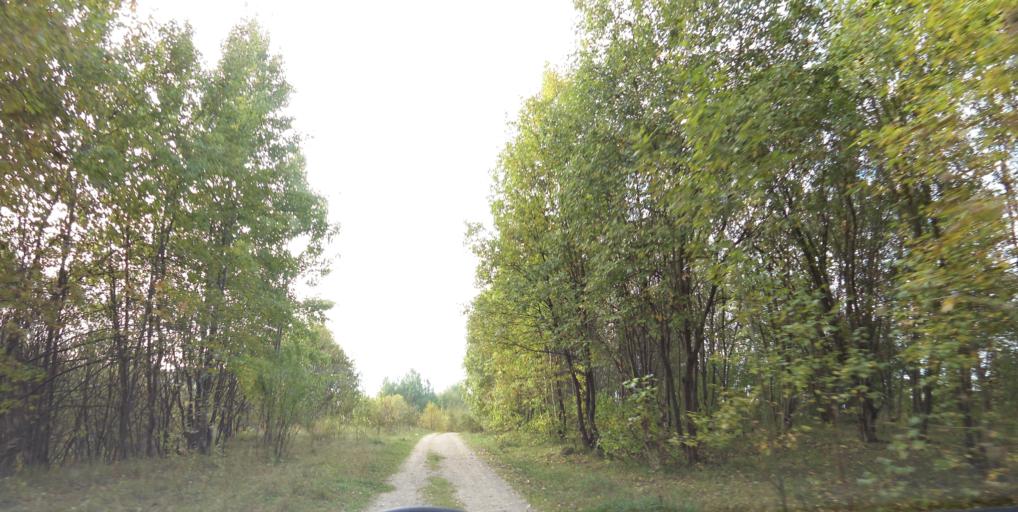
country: LT
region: Vilnius County
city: Justiniskes
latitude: 54.7172
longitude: 25.2101
